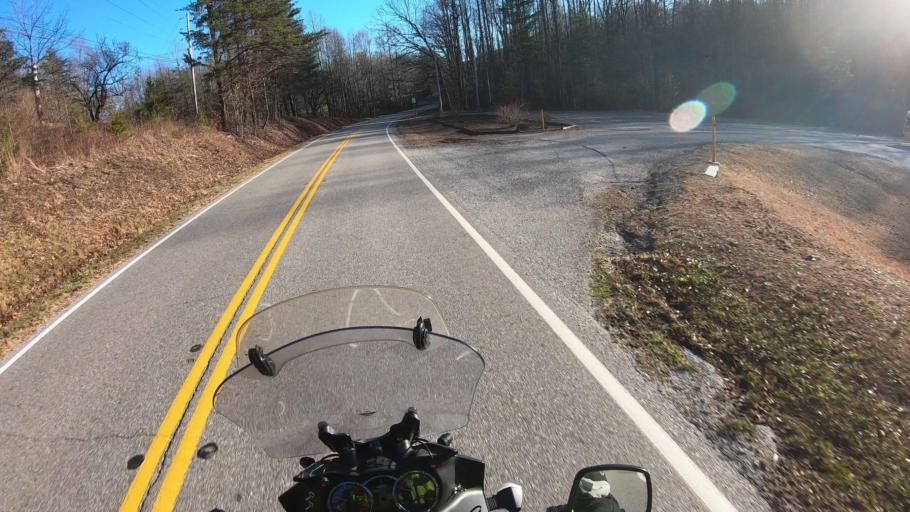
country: US
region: Georgia
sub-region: Lumpkin County
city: Dahlonega
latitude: 34.7033
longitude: -84.0349
